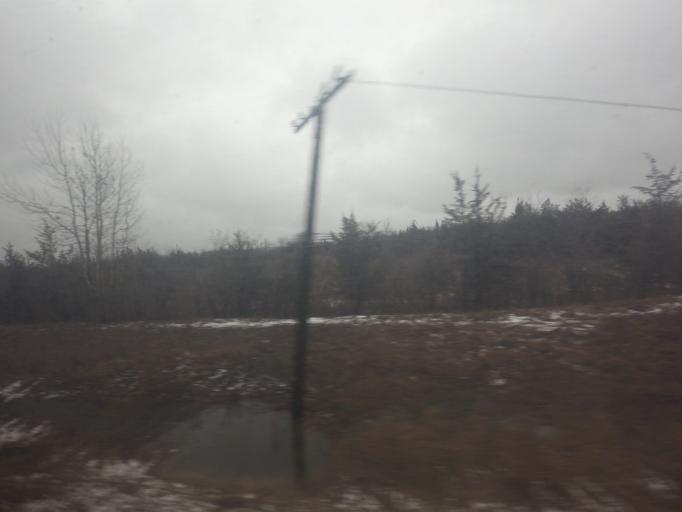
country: CA
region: Ontario
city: Deseronto
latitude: 44.2249
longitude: -77.0854
